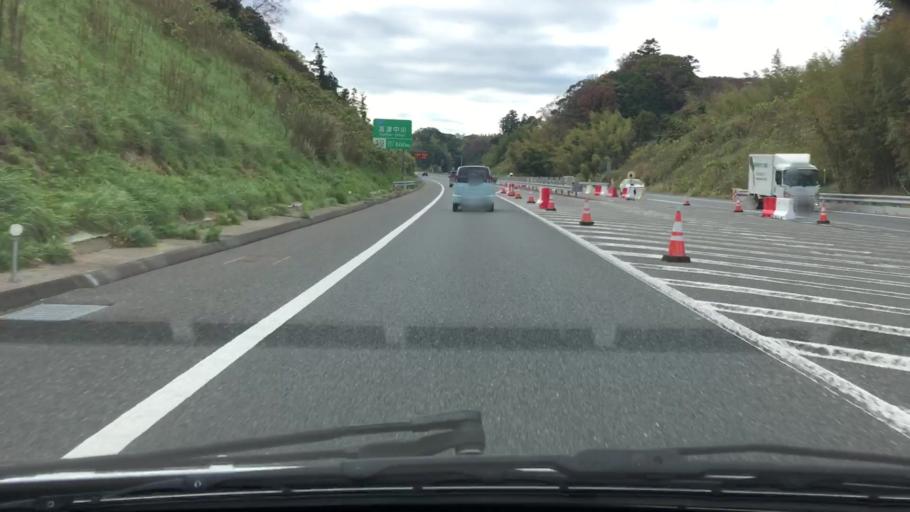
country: JP
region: Chiba
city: Kimitsu
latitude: 35.2592
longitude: 139.8958
